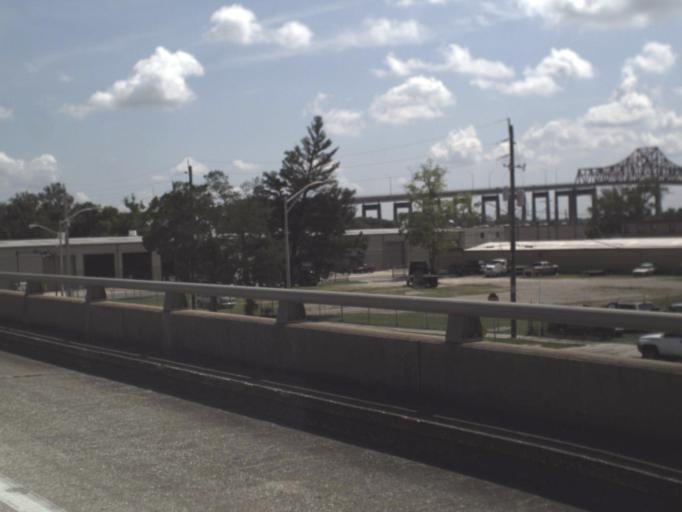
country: US
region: Florida
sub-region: Duval County
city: Jacksonville
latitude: 30.3237
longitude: -81.6344
